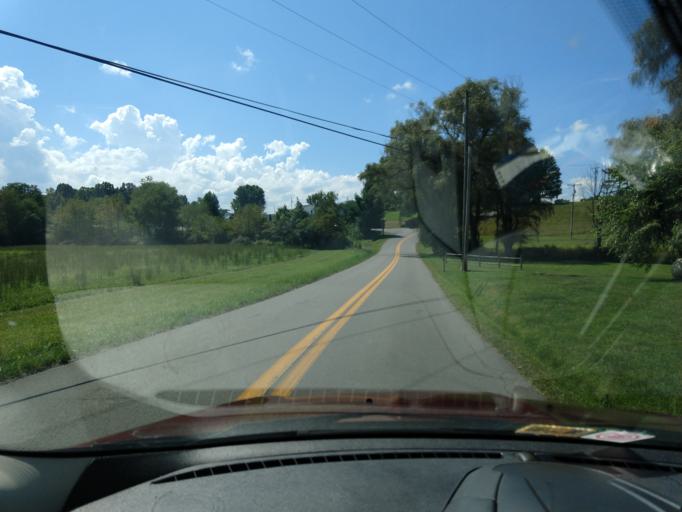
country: US
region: West Virginia
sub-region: Nicholas County
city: Summersville
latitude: 38.2794
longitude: -80.7636
